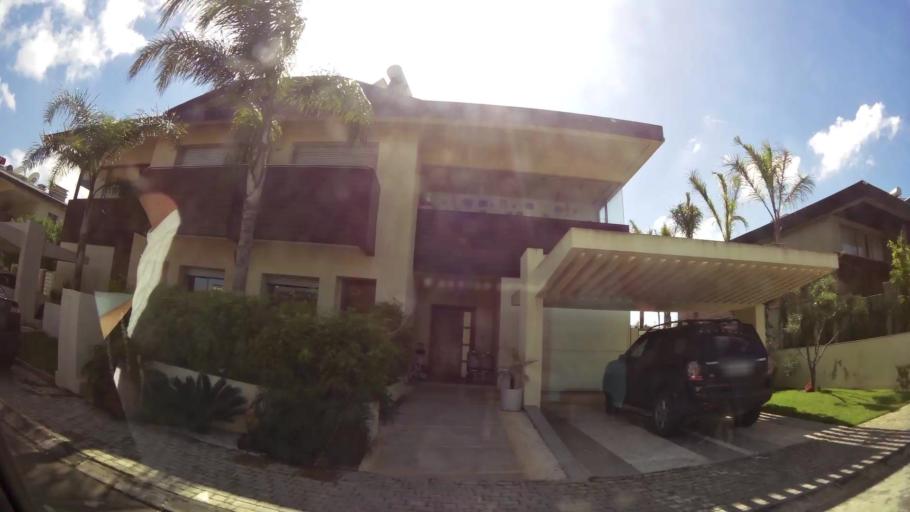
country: MA
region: Grand Casablanca
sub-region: Nouaceur
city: Bouskoura
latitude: 33.4673
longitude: -7.5955
